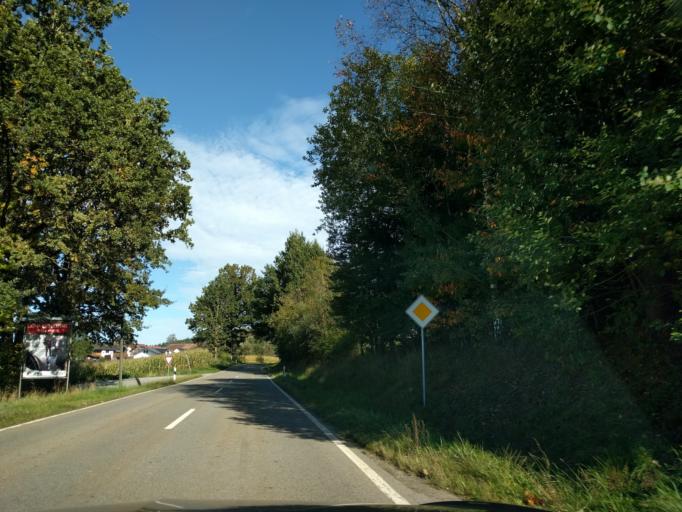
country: DE
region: Bavaria
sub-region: Lower Bavaria
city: Viechtach
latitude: 49.1003
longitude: 12.8866
